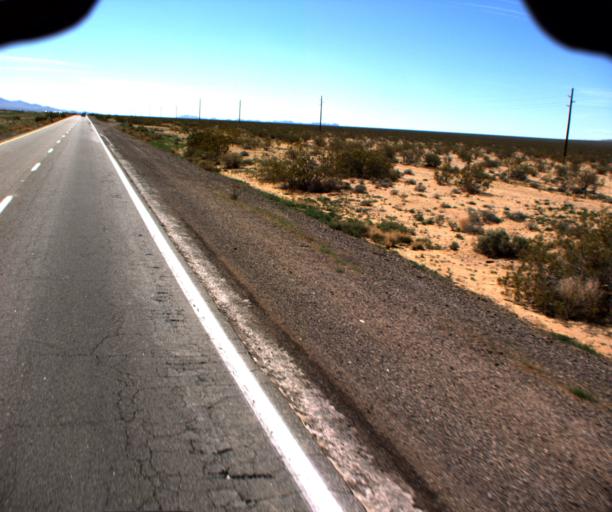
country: US
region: Arizona
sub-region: Mohave County
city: Dolan Springs
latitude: 35.6328
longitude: -114.4287
